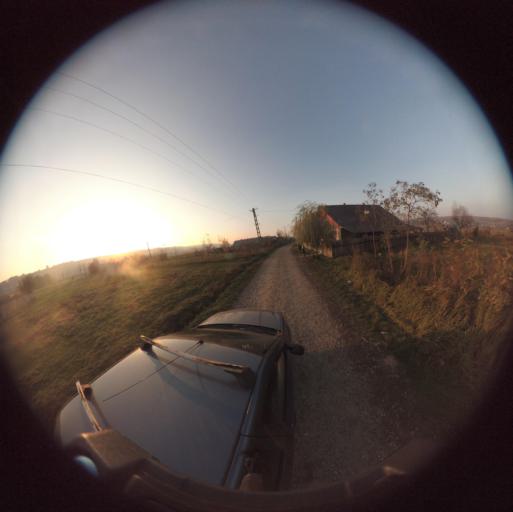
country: RO
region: Vaslui
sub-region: Comuna Bacesti
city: Bacesti
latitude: 46.8315
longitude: 27.2464
